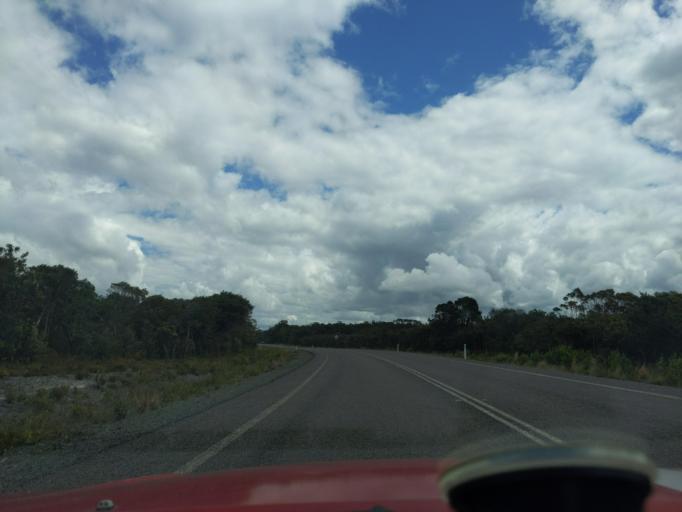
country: AU
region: New South Wales
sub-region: Great Lakes
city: Hawks Nest
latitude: -32.5900
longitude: 152.2701
